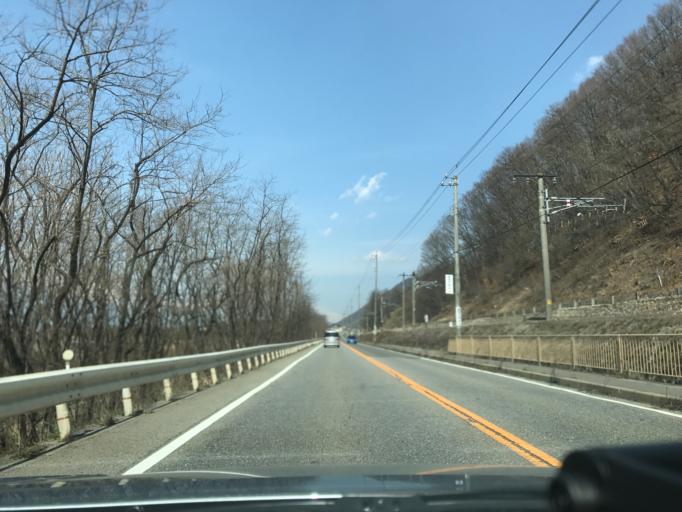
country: JP
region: Nagano
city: Toyoshina
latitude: 36.2887
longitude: 137.9447
